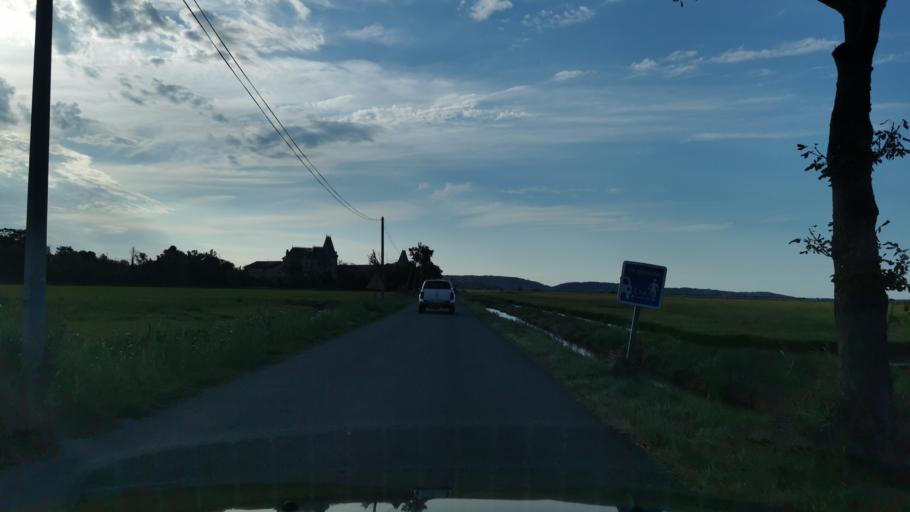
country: FR
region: Languedoc-Roussillon
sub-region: Departement de l'Aude
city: Gruissan
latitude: 43.1216
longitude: 3.0321
